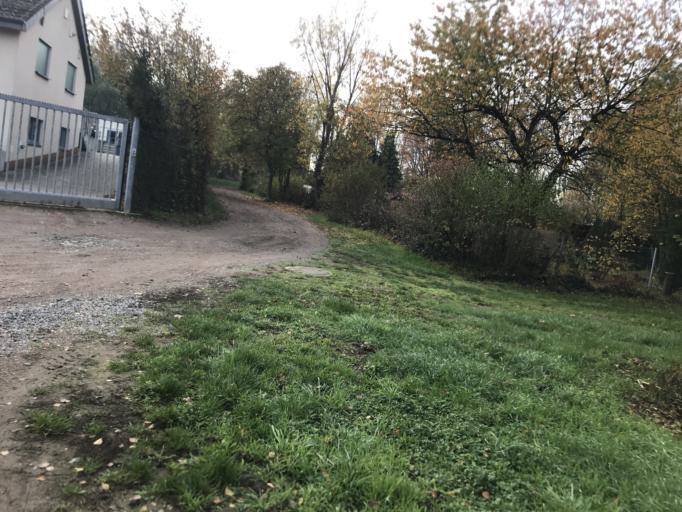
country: DE
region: Hesse
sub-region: Regierungsbezirk Darmstadt
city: Trebur
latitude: 49.9240
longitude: 8.3980
